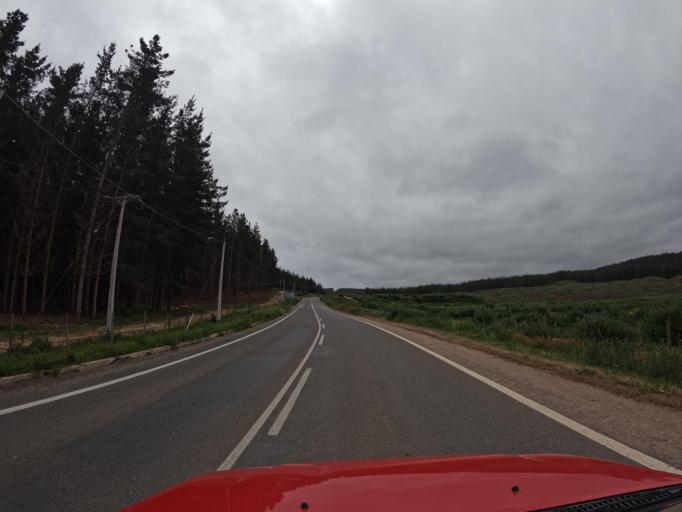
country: CL
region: O'Higgins
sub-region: Provincia de Colchagua
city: Santa Cruz
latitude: -34.6397
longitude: -72.0343
